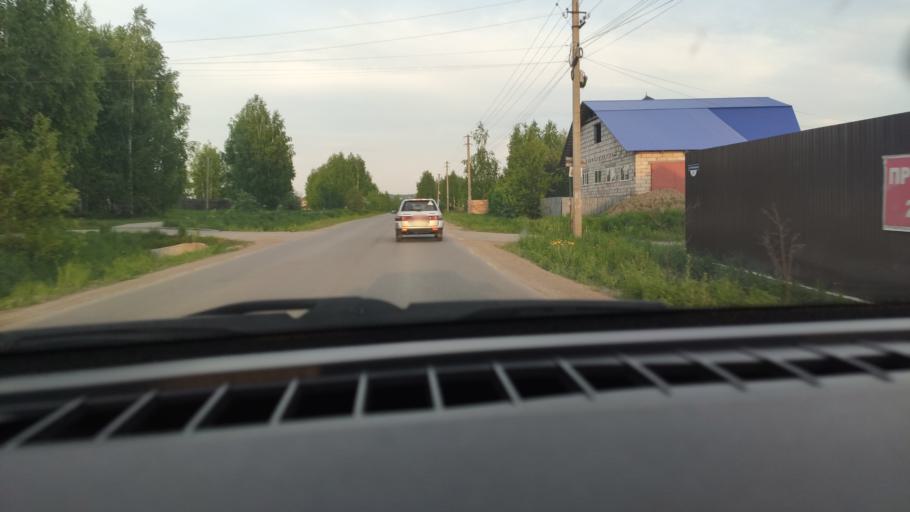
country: RU
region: Perm
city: Kondratovo
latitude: 58.0572
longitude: 56.0089
